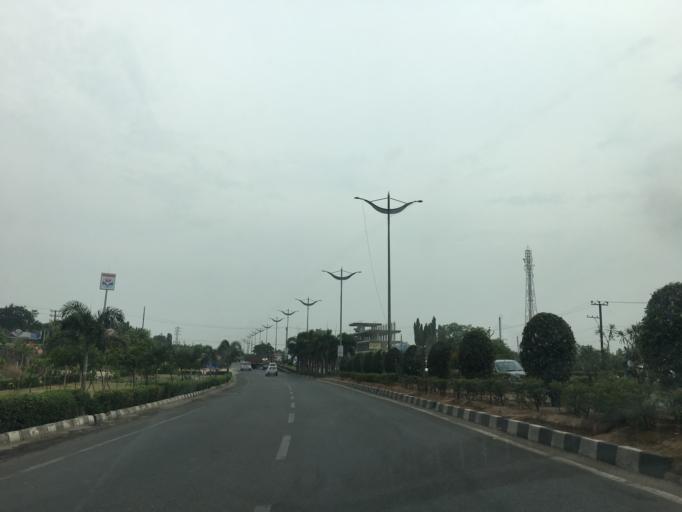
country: IN
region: Telangana
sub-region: Rangareddi
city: Balapur
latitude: 17.2951
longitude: 78.4179
